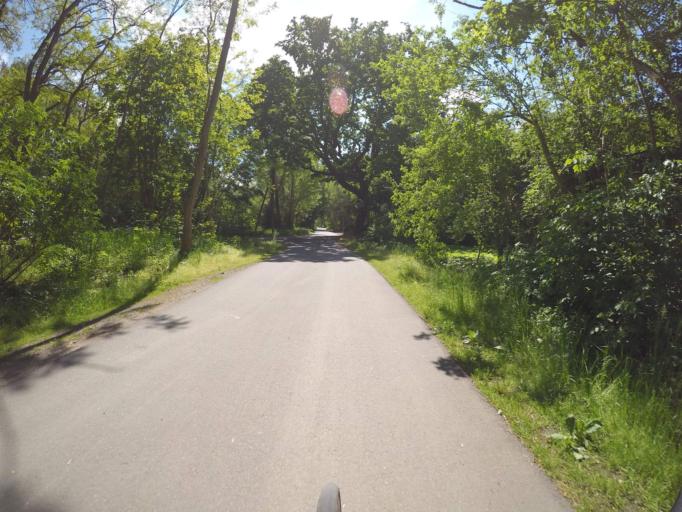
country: DE
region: Brandenburg
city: Werder
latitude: 52.4059
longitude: 12.9501
